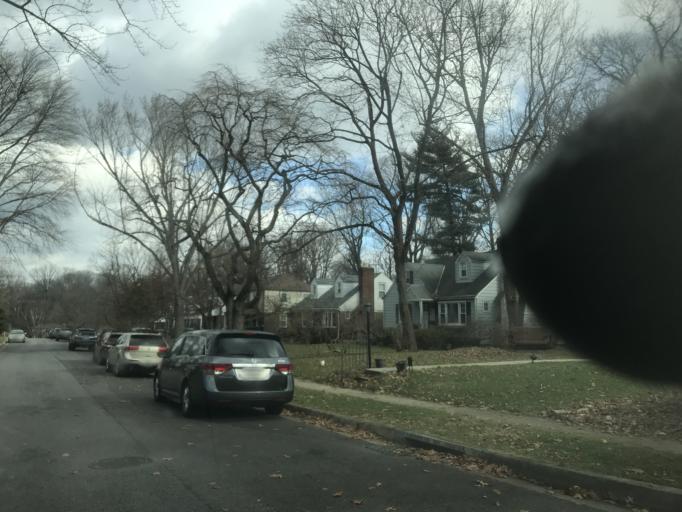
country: US
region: Maryland
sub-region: Baltimore County
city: Towson
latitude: 39.3962
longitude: -76.5885
